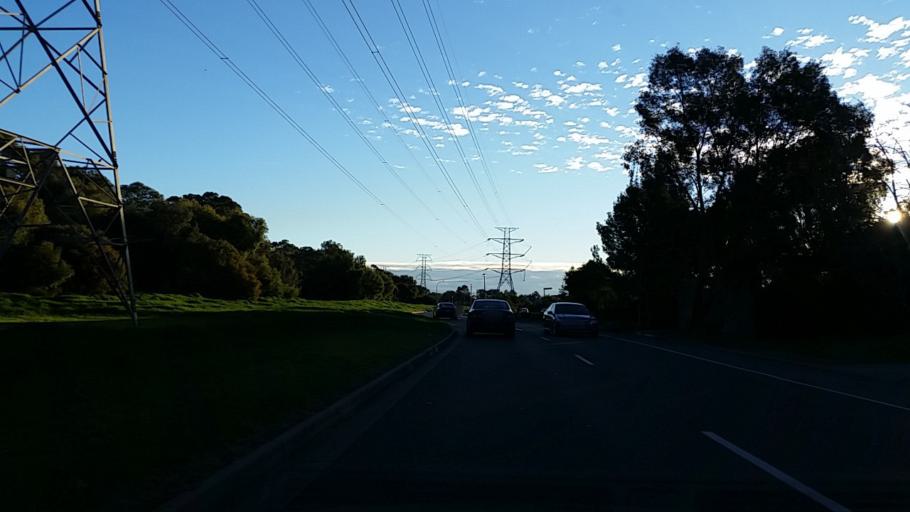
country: AU
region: South Australia
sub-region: Salisbury
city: Salisbury
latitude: -34.7600
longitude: 138.6249
